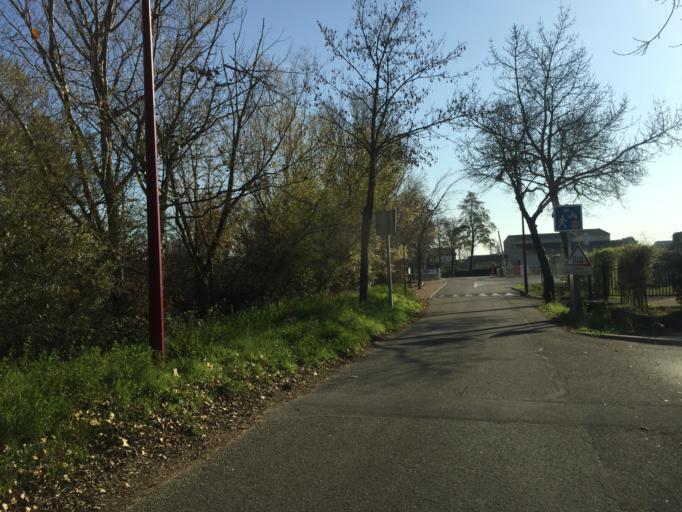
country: FR
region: Provence-Alpes-Cote d'Azur
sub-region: Departement du Vaucluse
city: Entraigues-sur-la-Sorgue
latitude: 44.0077
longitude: 4.9283
